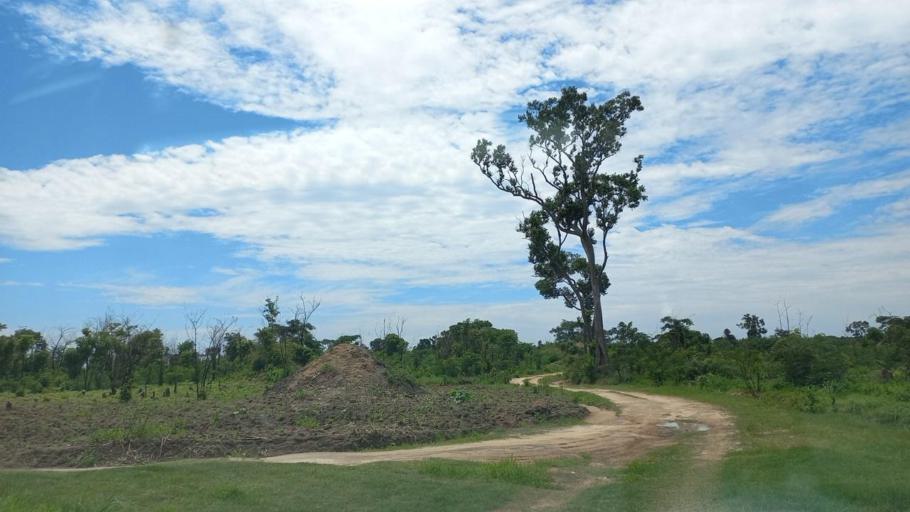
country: ZM
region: Copperbelt
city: Kitwe
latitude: -12.8087
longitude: 28.4010
